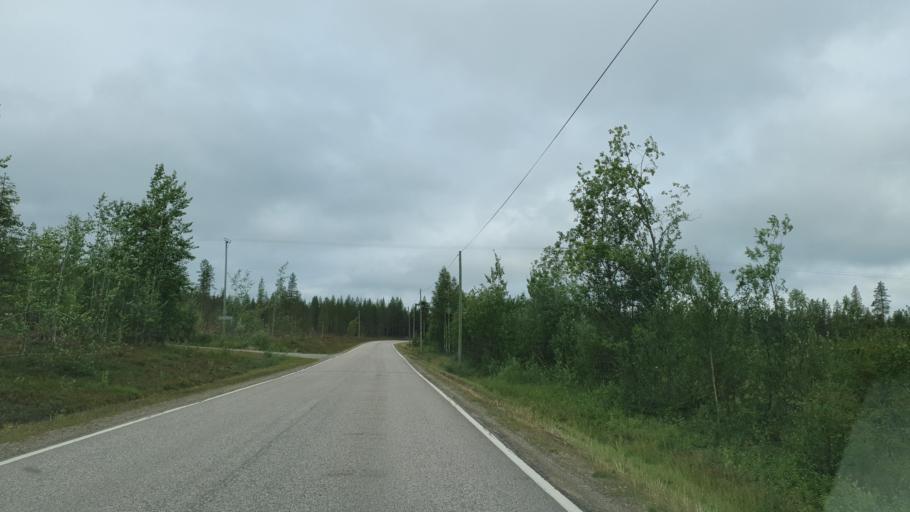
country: FI
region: Lapland
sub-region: Pohjois-Lappi
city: Sodankylae
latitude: 67.4158
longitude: 26.2997
